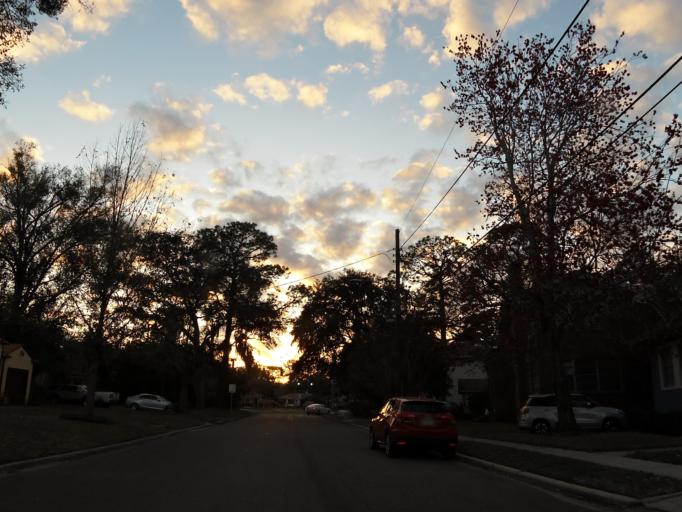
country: US
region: Florida
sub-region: Duval County
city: Jacksonville
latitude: 30.3094
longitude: -81.7044
